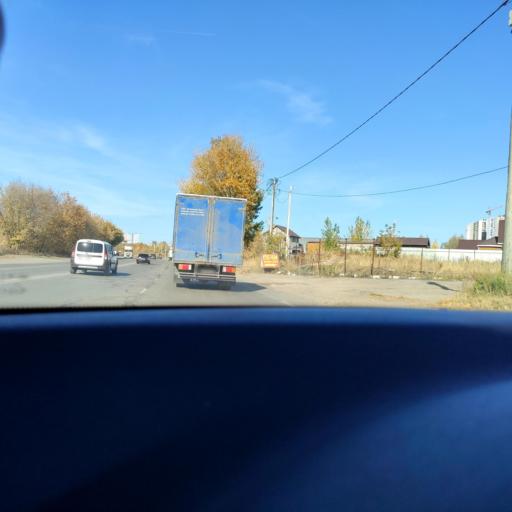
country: RU
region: Samara
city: Petra-Dubrava
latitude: 53.2685
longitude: 50.2801
